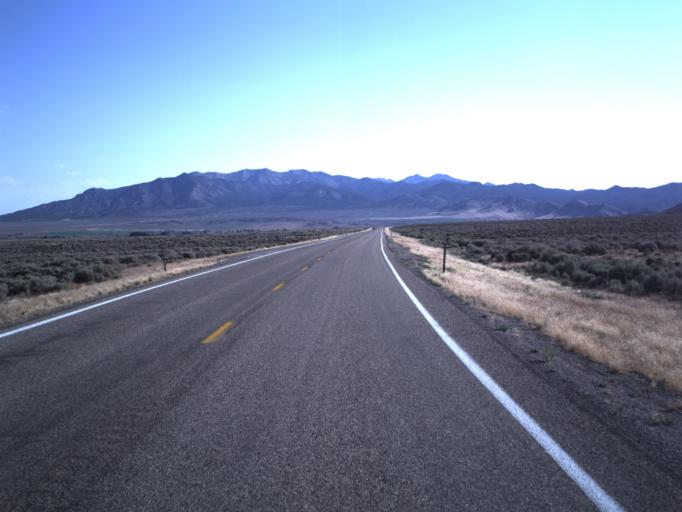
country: US
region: Utah
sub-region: Beaver County
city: Milford
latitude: 38.1703
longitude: -112.9527
